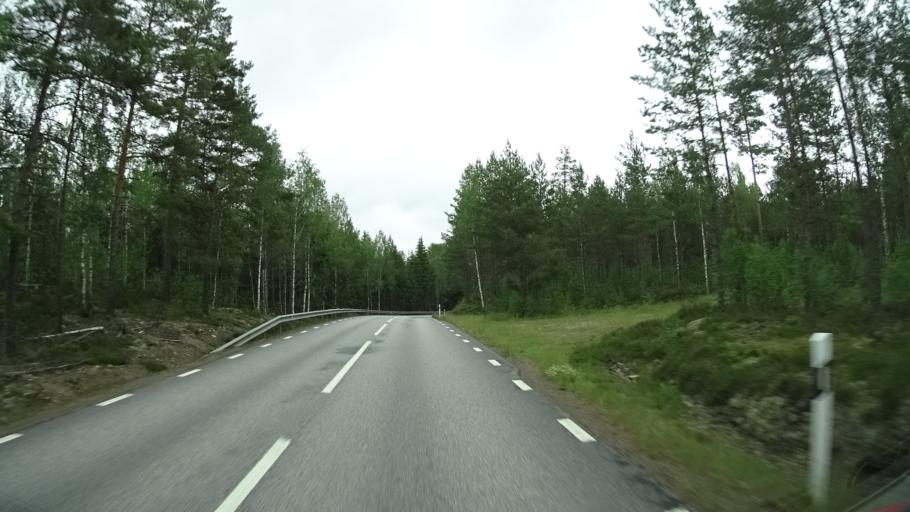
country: SE
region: Joenkoeping
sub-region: Eksjo Kommun
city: Mariannelund
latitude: 57.5720
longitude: 15.6999
